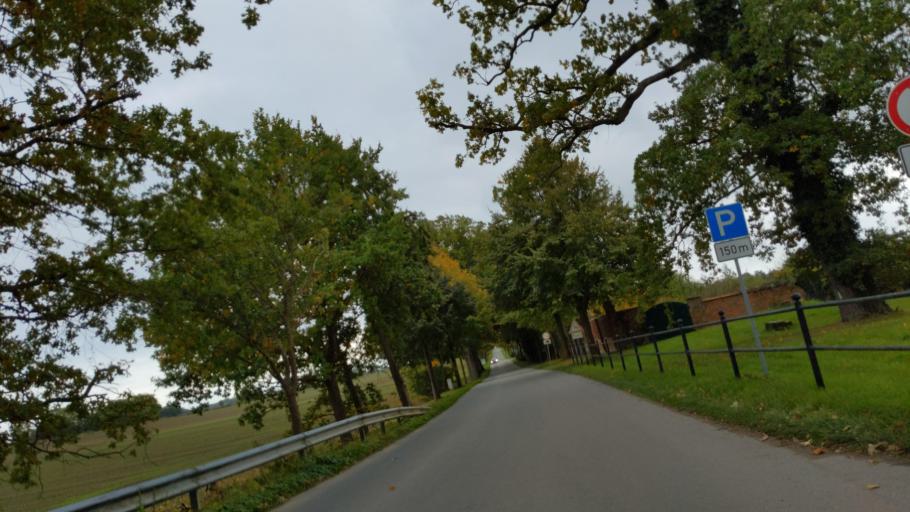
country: DE
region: Schleswig-Holstein
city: Neustadt in Holstein
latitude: 54.1287
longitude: 10.7769
